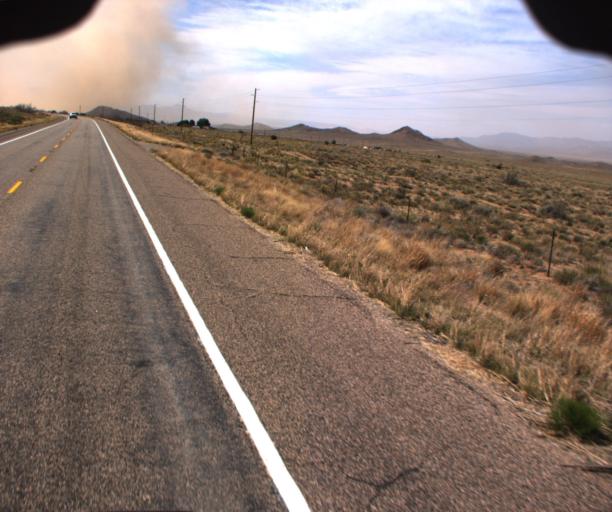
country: US
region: Arizona
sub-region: Mohave County
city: New Kingman-Butler
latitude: 35.4163
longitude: -113.7929
